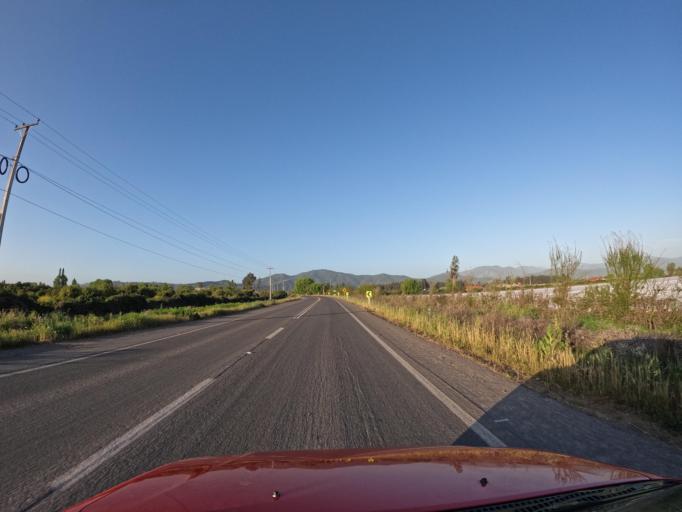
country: CL
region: O'Higgins
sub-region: Provincia de Cachapoal
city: San Vicente
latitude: -34.2949
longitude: -71.3699
